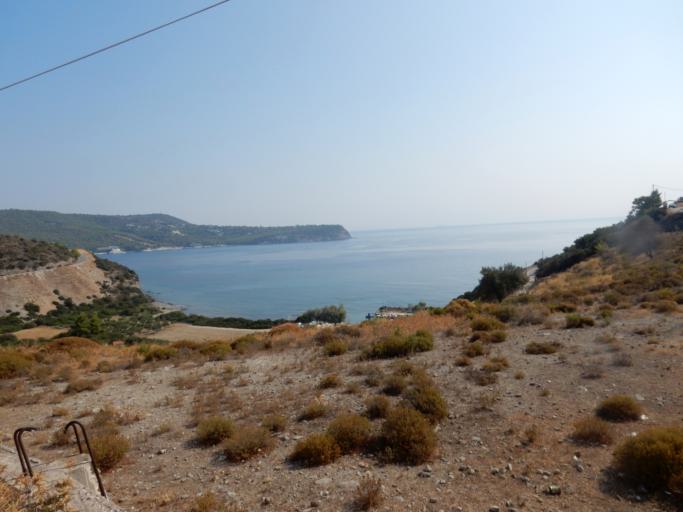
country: GR
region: Attica
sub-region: Nomos Piraios
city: Vathi
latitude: 37.7295
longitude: 23.5383
